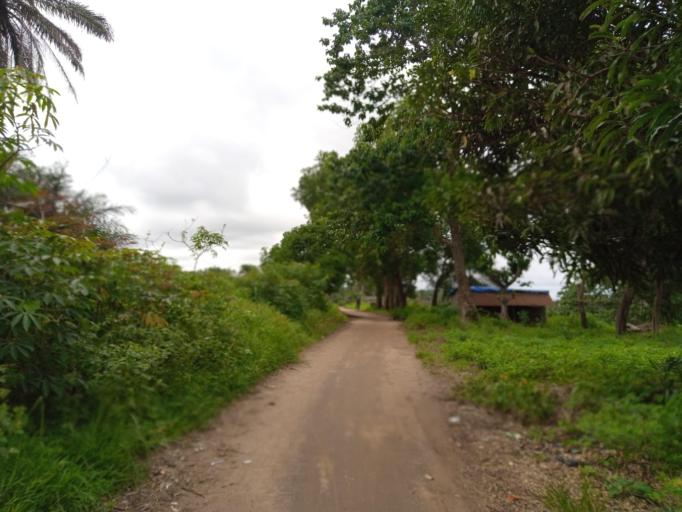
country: SL
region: Northern Province
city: Masoyila
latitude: 8.5860
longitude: -13.1954
